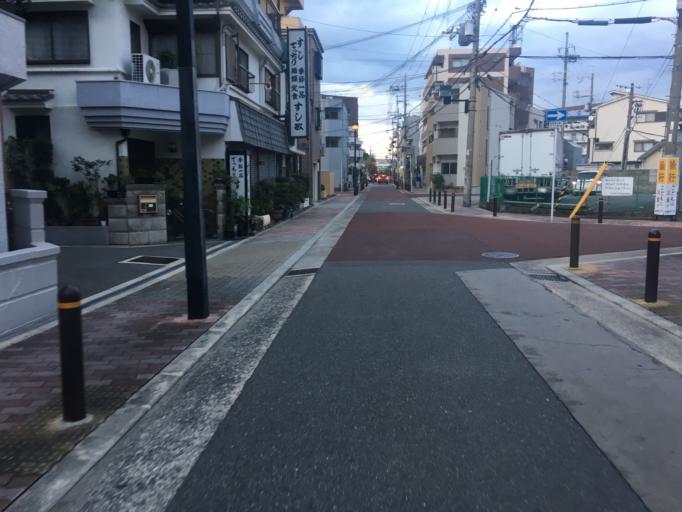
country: JP
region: Osaka
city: Moriguchi
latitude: 34.7475
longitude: 135.5430
